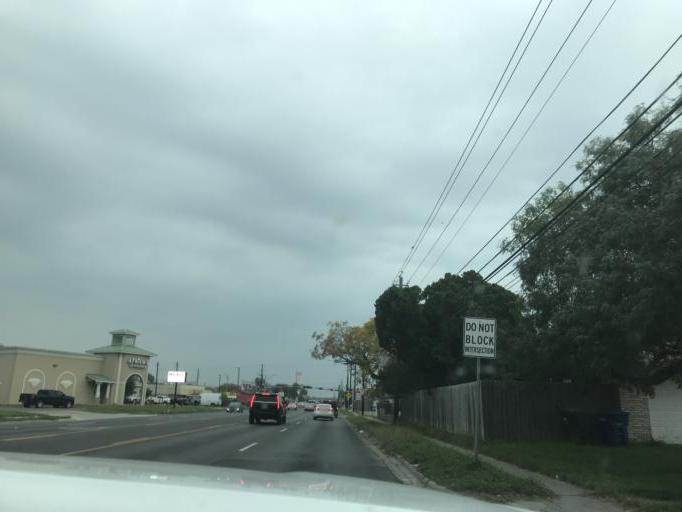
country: US
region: Texas
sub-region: Nueces County
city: Corpus Christi
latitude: 27.6984
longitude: -97.3630
